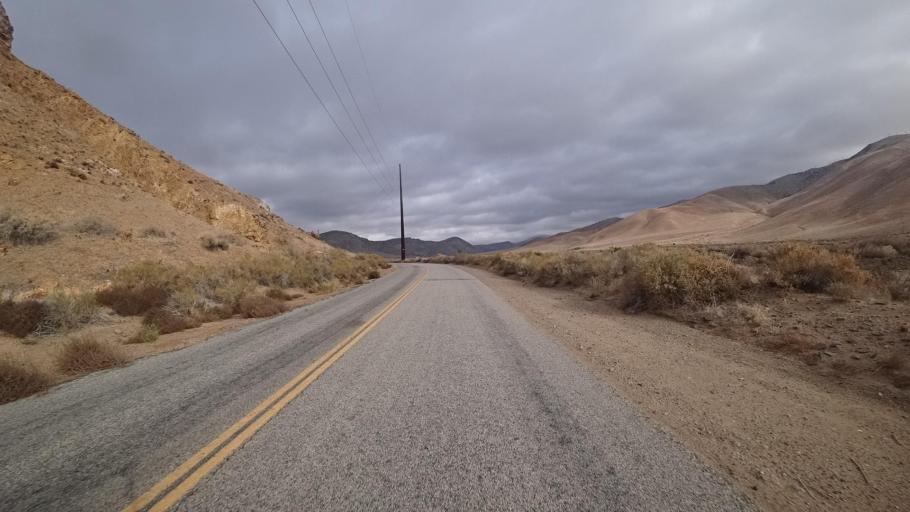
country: US
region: California
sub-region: Kern County
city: Tehachapi
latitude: 35.1137
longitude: -118.3234
